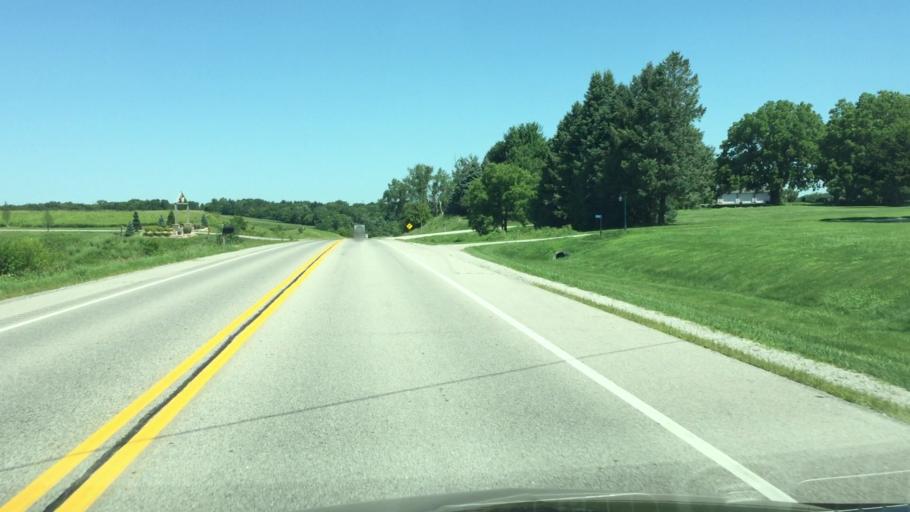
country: US
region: Iowa
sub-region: Johnson County
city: Solon
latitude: 41.7631
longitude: -91.4804
